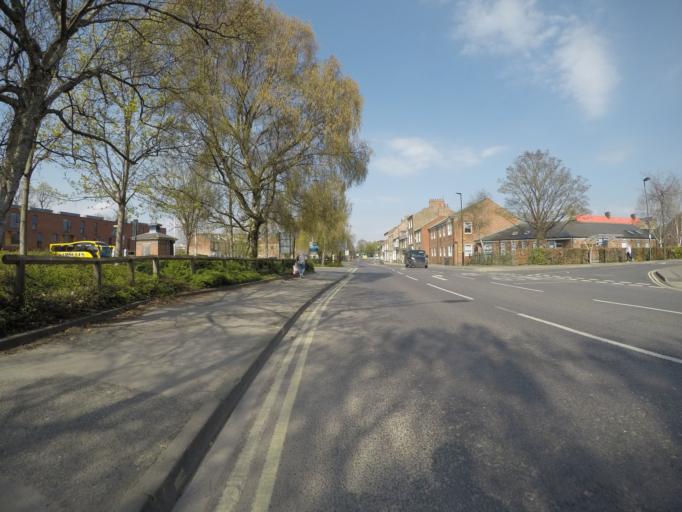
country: GB
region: England
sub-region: City of York
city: York
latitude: 53.9661
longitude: -1.0831
